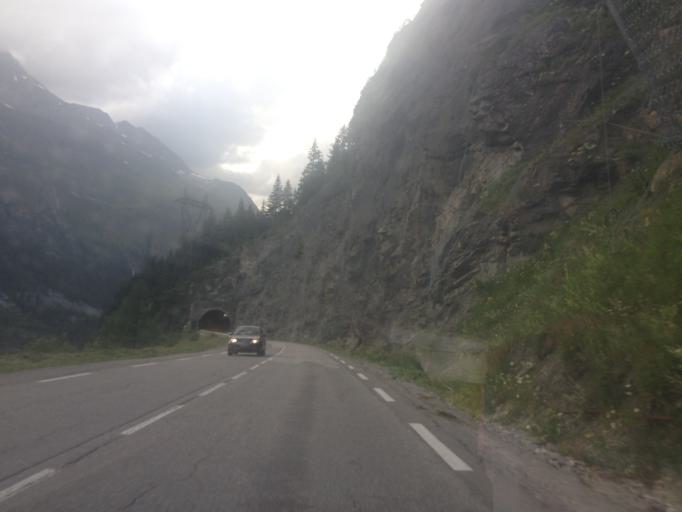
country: FR
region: Rhone-Alpes
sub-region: Departement de la Savoie
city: Tignes
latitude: 45.5040
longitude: 6.9297
